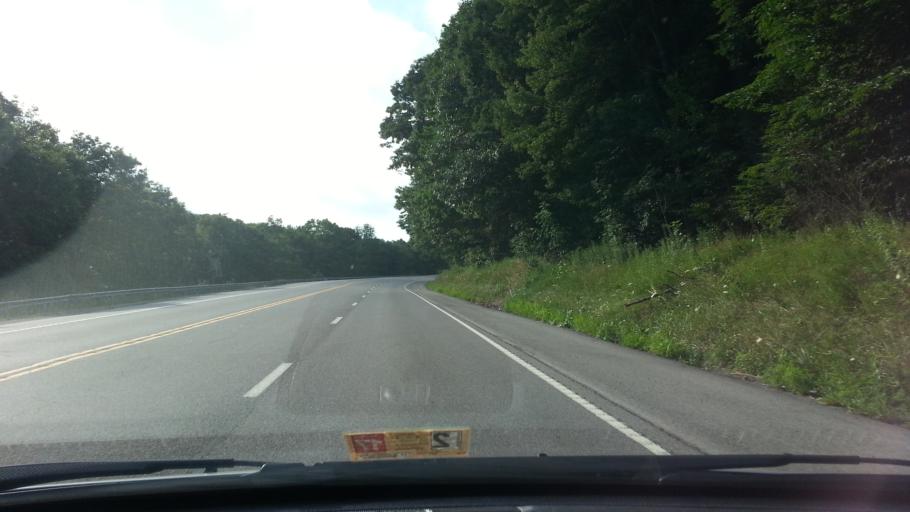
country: US
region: Pennsylvania
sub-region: Elk County
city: Saint Marys
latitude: 41.3047
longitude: -78.5047
